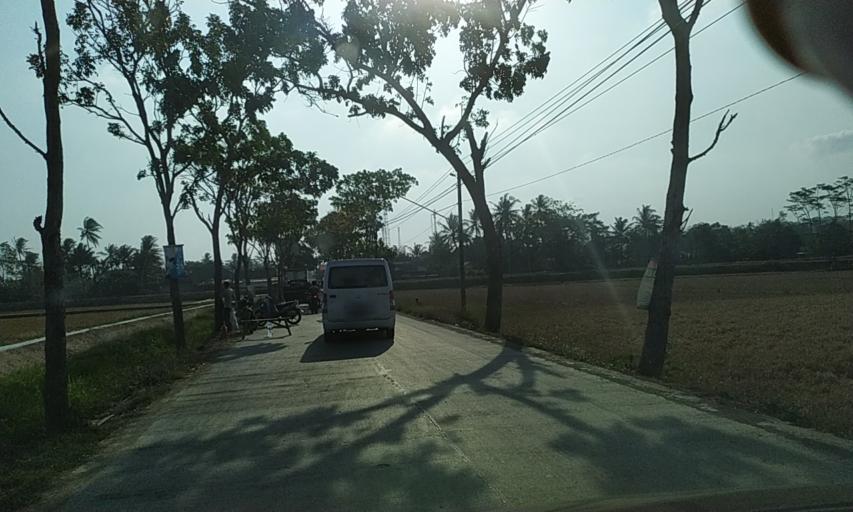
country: ID
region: Central Java
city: Madusari
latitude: -7.6226
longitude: 109.0812
